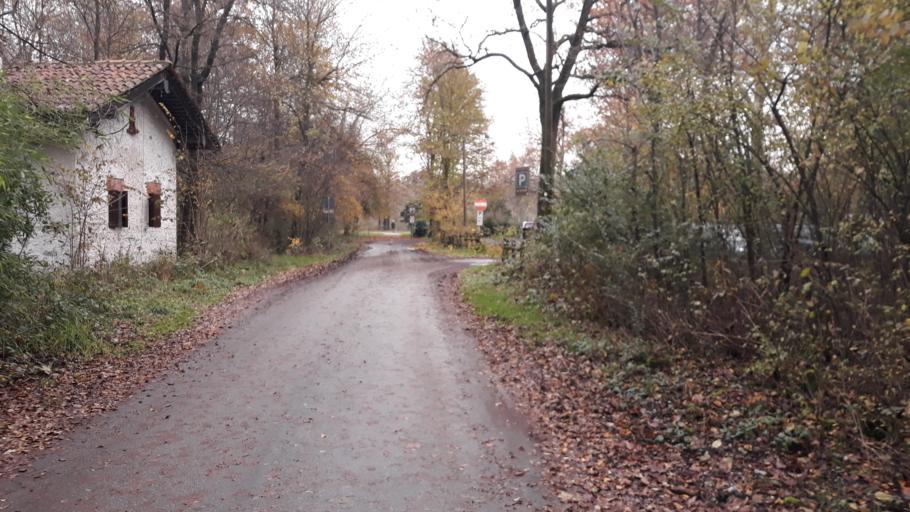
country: IT
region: Lombardy
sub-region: Citta metropolitana di Milano
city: Nosate
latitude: 45.5405
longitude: 8.7091
